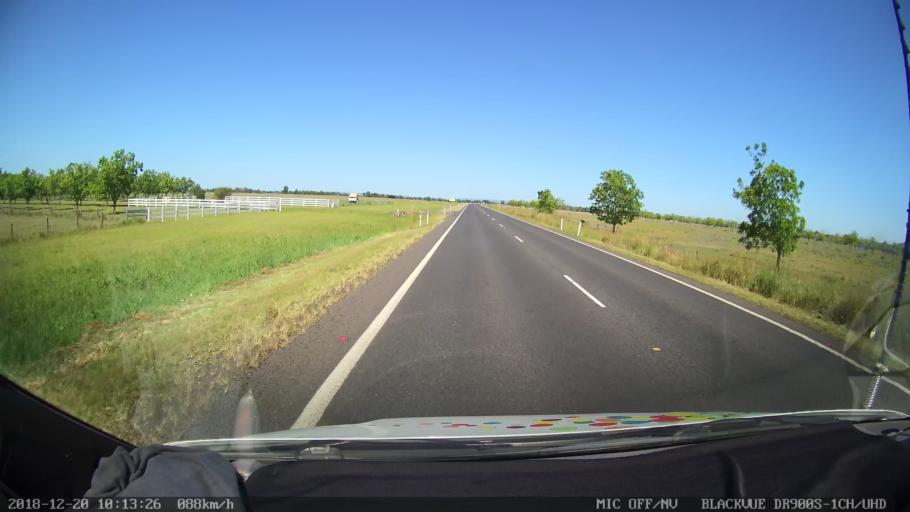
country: AU
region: New South Wales
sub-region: Richmond Valley
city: Casino
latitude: -28.8731
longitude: 153.1301
